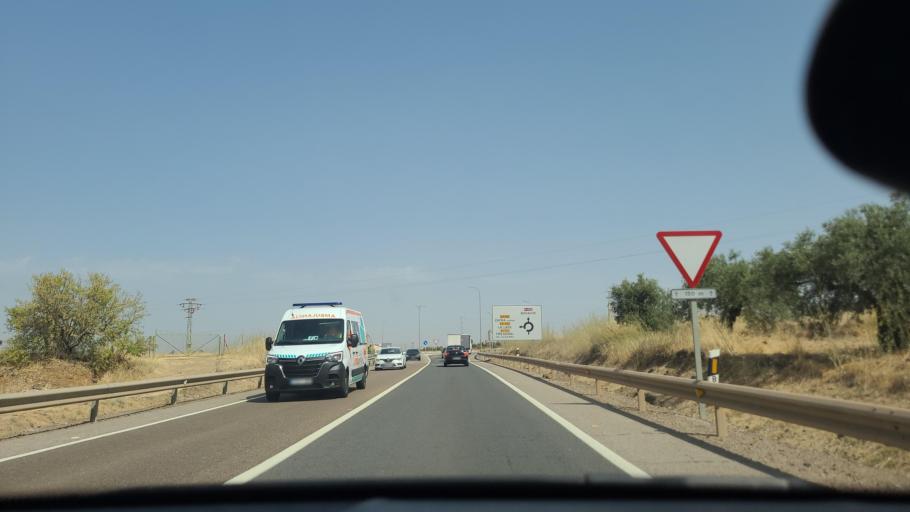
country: ES
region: Extremadura
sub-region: Provincia de Badajoz
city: Zafra
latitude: 38.4377
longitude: -6.4237
